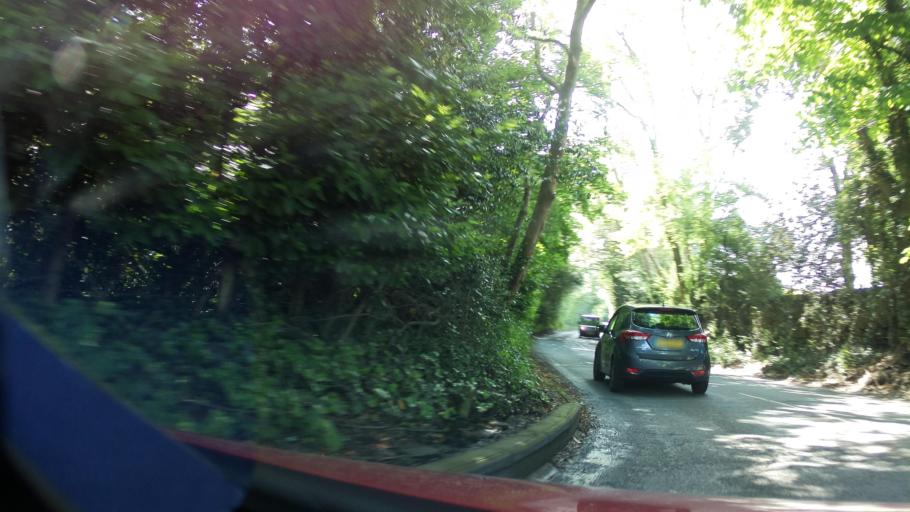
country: GB
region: England
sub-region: Hertfordshire
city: Chorleywood
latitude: 51.6587
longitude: -0.4578
